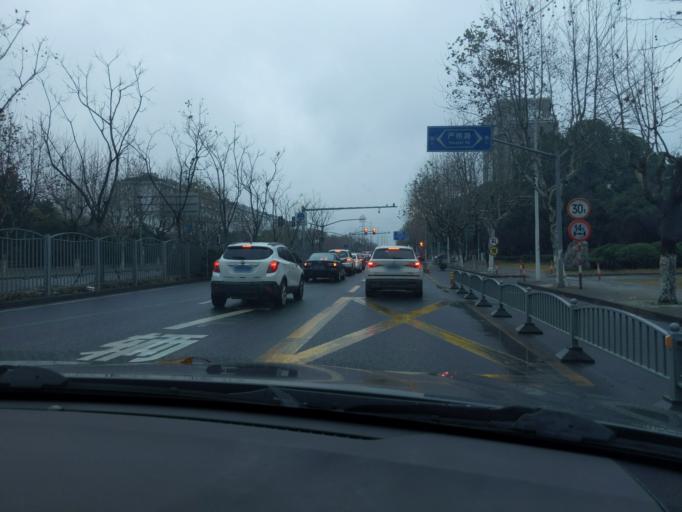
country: CN
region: Shanghai Shi
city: Huamu
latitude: 31.1895
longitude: 121.5237
